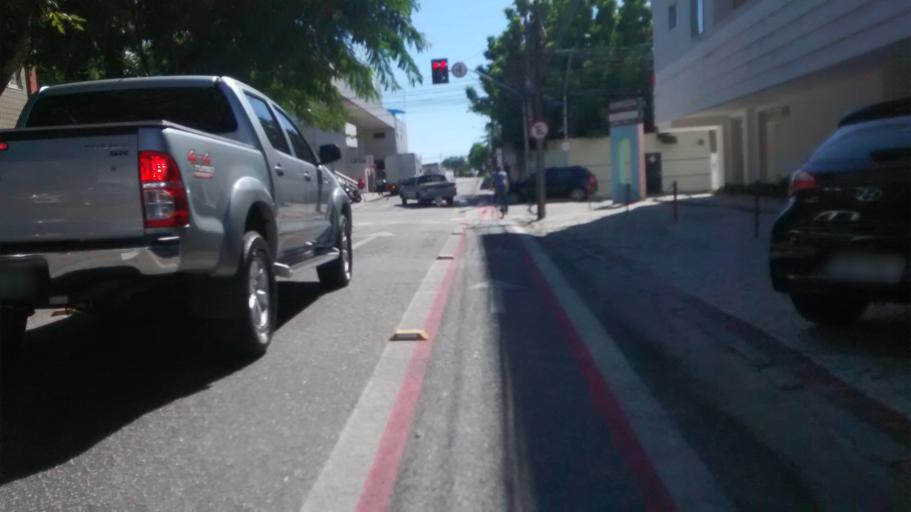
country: BR
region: Ceara
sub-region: Fortaleza
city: Fortaleza
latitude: -3.7407
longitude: -38.5154
